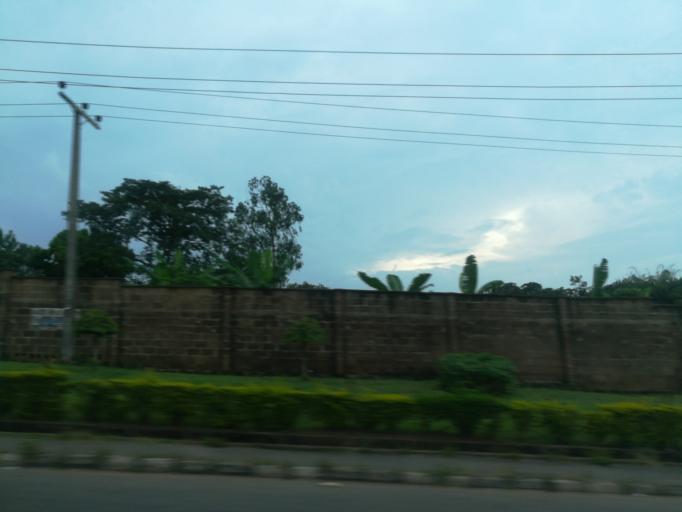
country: NG
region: Oyo
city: Ibadan
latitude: 7.4488
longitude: 3.9069
